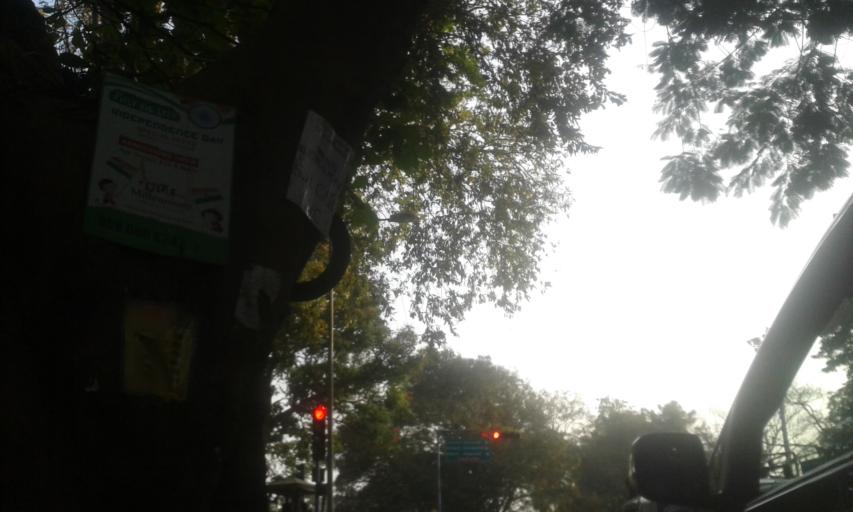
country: IN
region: Karnataka
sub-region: Bangalore Urban
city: Bangalore
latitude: 12.9106
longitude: 77.5952
